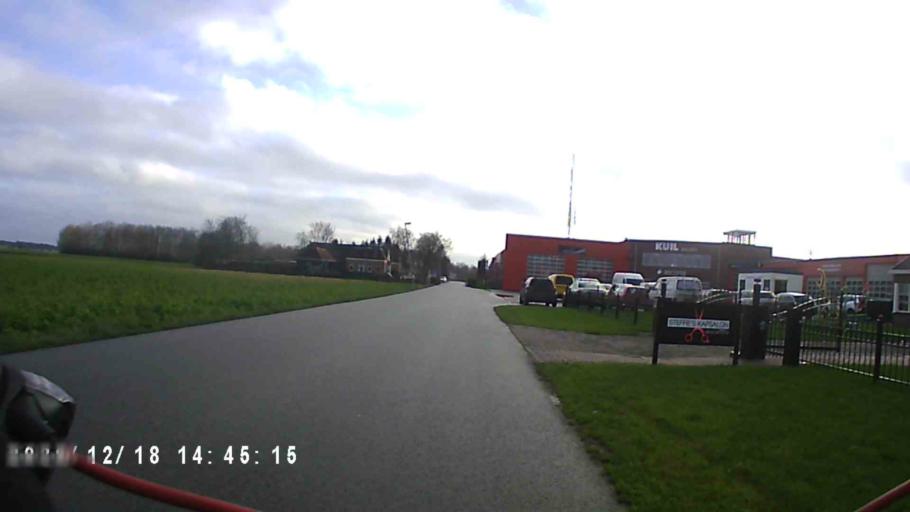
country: NL
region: Groningen
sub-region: Gemeente Haren
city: Haren
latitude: 53.2017
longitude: 6.6581
